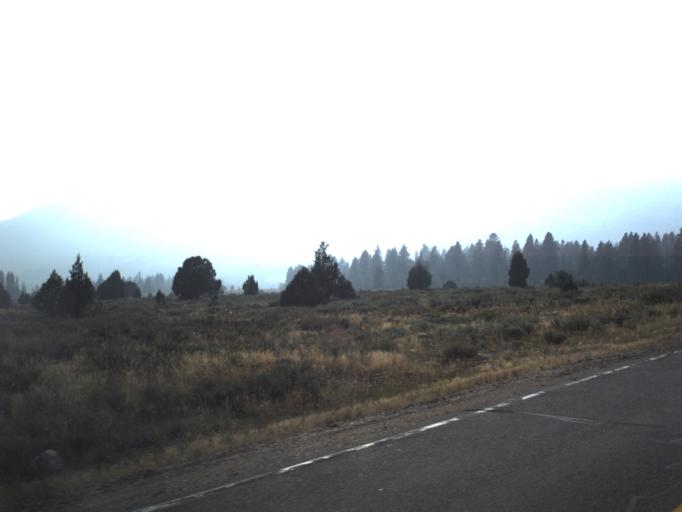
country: US
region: Utah
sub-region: Summit County
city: Francis
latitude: 40.5981
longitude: -111.0992
